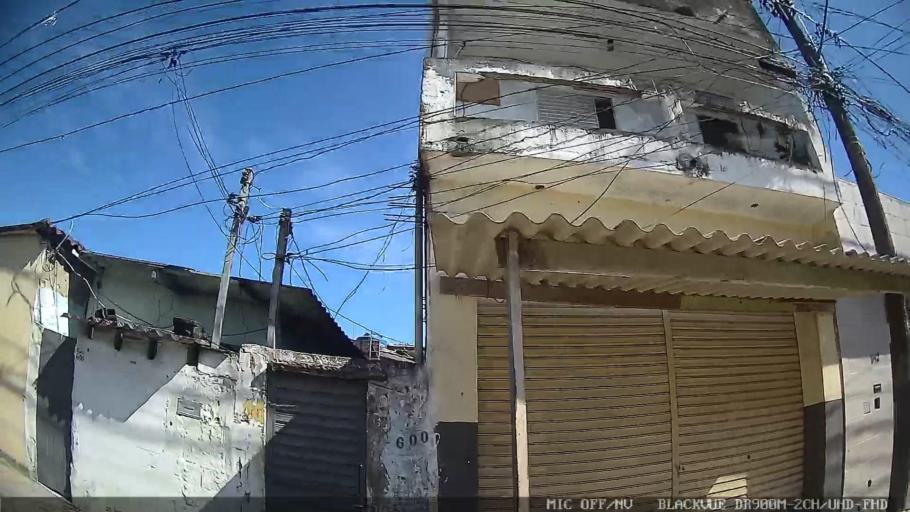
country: BR
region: Sao Paulo
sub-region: Santos
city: Santos
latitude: -23.9479
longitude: -46.2847
